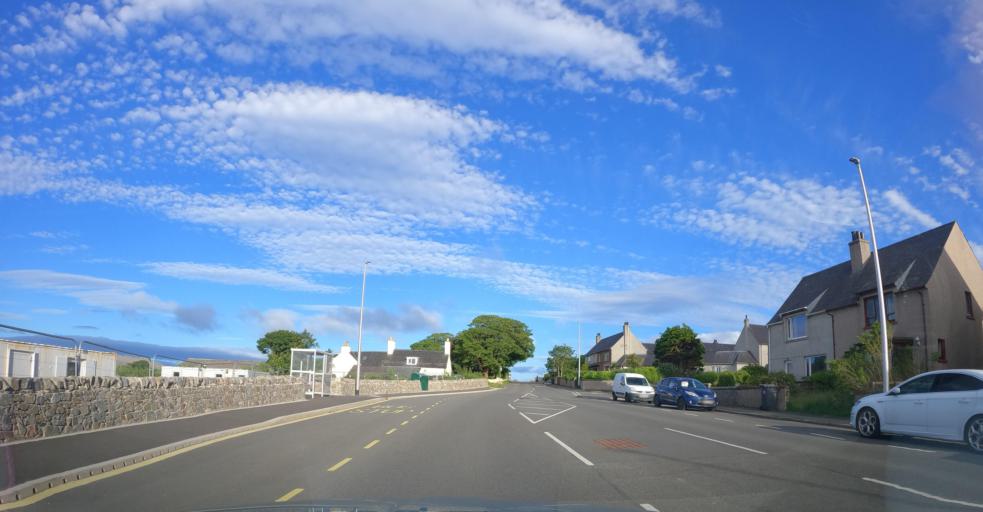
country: GB
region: Scotland
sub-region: Eilean Siar
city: Isle of Lewis
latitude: 58.2164
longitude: -6.3740
